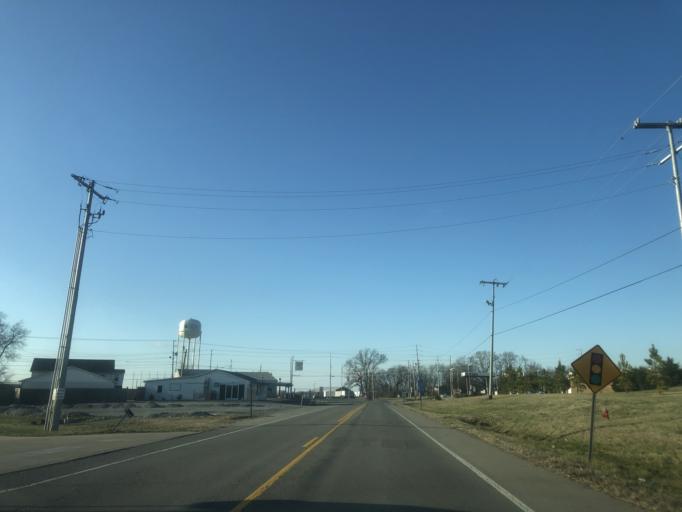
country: US
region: Tennessee
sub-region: Sumner County
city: Portland
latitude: 36.6317
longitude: -86.5630
